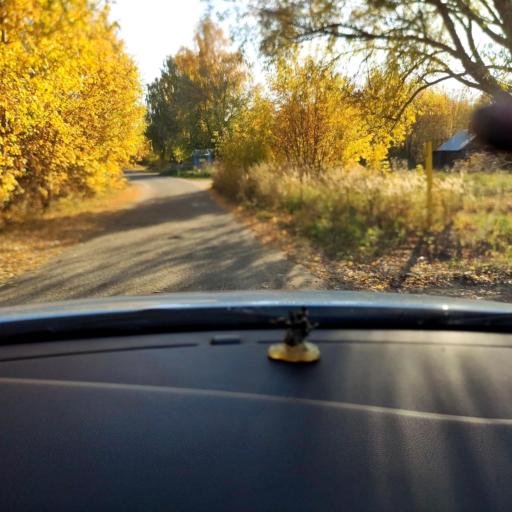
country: RU
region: Tatarstan
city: Stolbishchi
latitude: 55.6243
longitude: 49.1504
